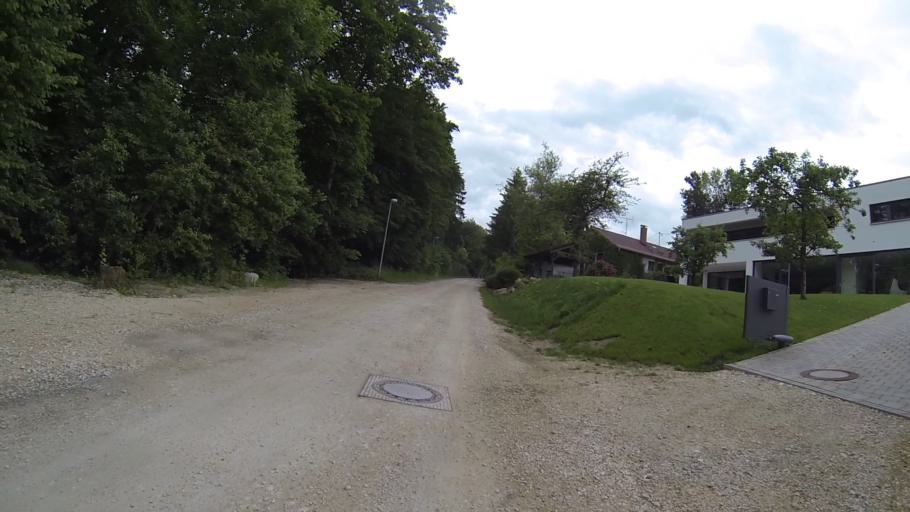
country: DE
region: Baden-Wuerttemberg
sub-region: Tuebingen Region
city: Dornstadt
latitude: 48.4209
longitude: 9.8863
